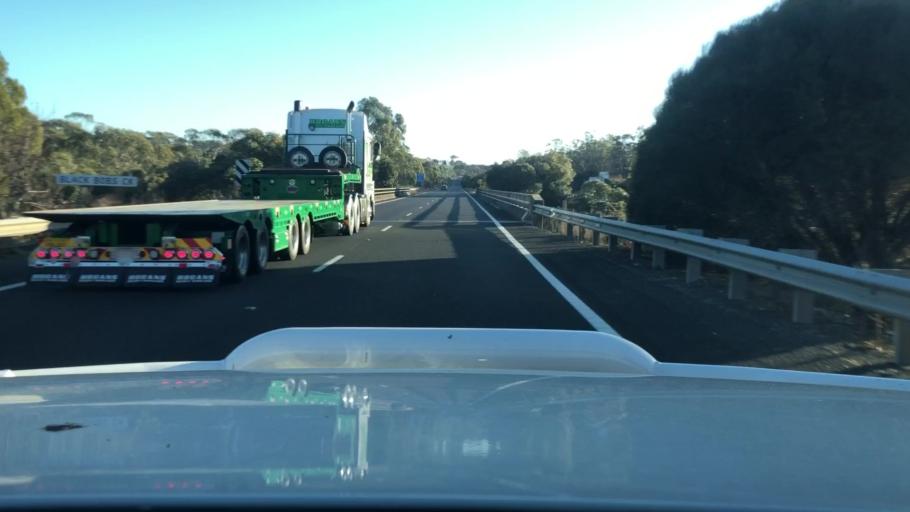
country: AU
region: New South Wales
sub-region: Wingecarribee
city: Bundanoon
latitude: -34.5761
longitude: 150.2530
